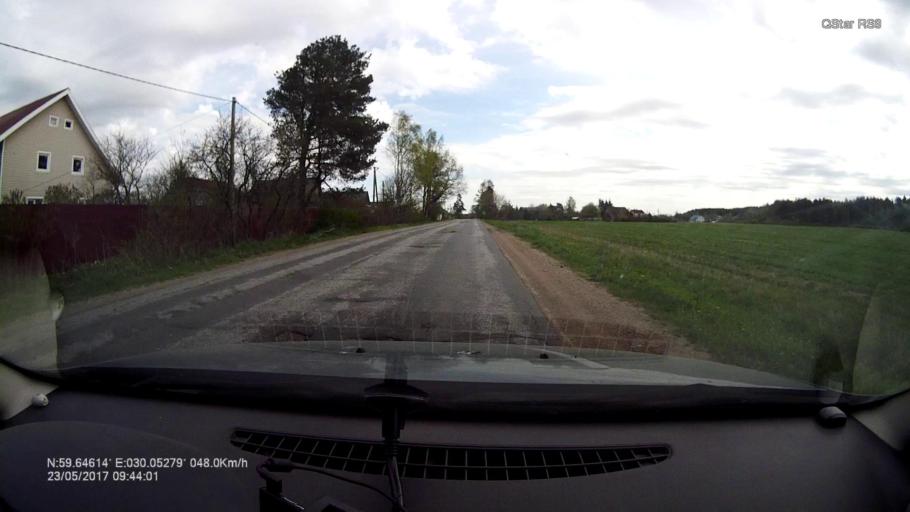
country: RU
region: Leningrad
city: Taytsy
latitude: 59.6462
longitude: 30.0528
